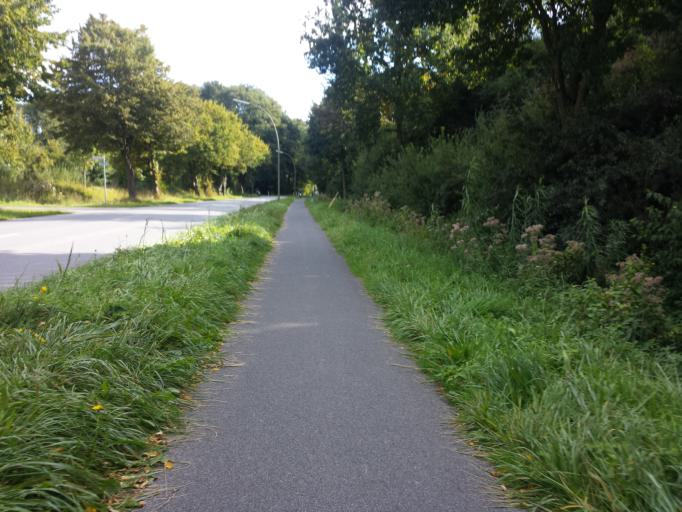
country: DE
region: North Rhine-Westphalia
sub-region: Regierungsbezirk Detmold
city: Langenberg
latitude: 51.7592
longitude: 8.3230
